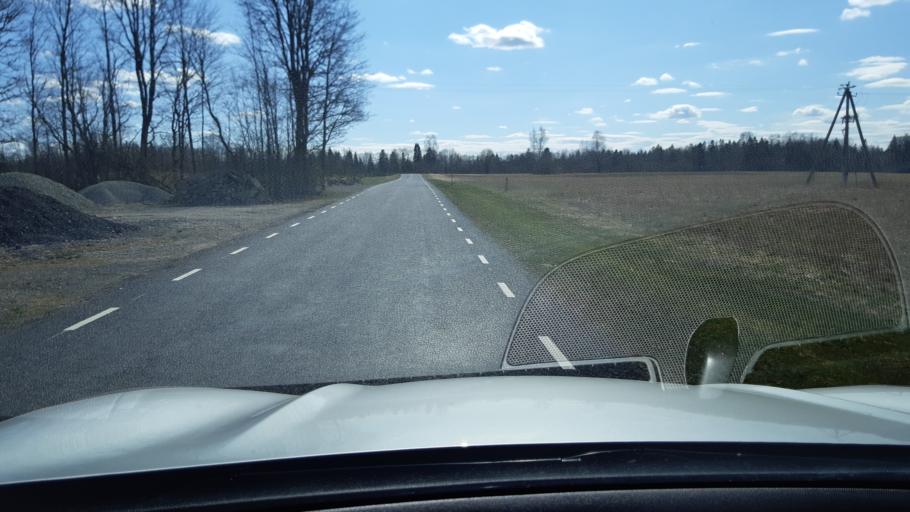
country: EE
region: Harju
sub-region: Rae vald
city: Vaida
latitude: 59.2217
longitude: 24.9662
